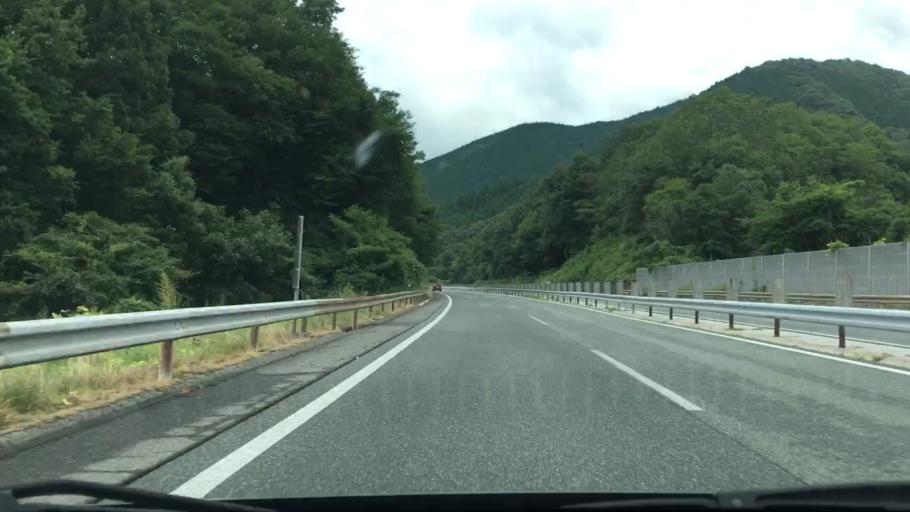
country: JP
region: Okayama
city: Niimi
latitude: 34.9606
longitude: 133.3318
